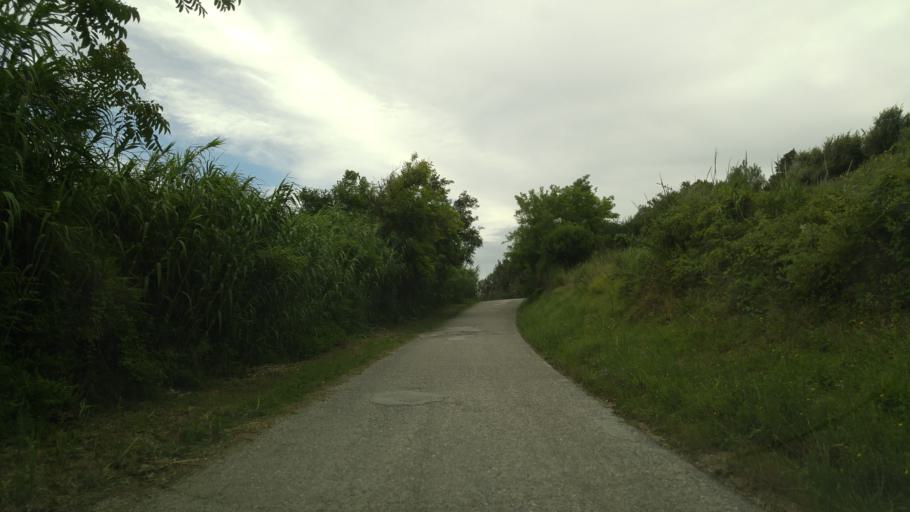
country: IT
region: The Marches
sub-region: Provincia di Pesaro e Urbino
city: Fenile
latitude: 43.8638
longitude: 12.9851
